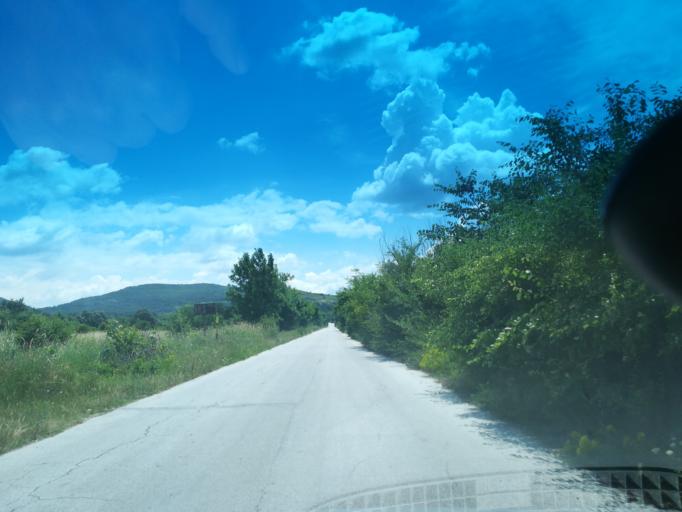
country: BG
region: Khaskovo
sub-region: Obshtina Mineralni Bani
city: Mineralni Bani
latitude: 41.9920
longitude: 25.2407
